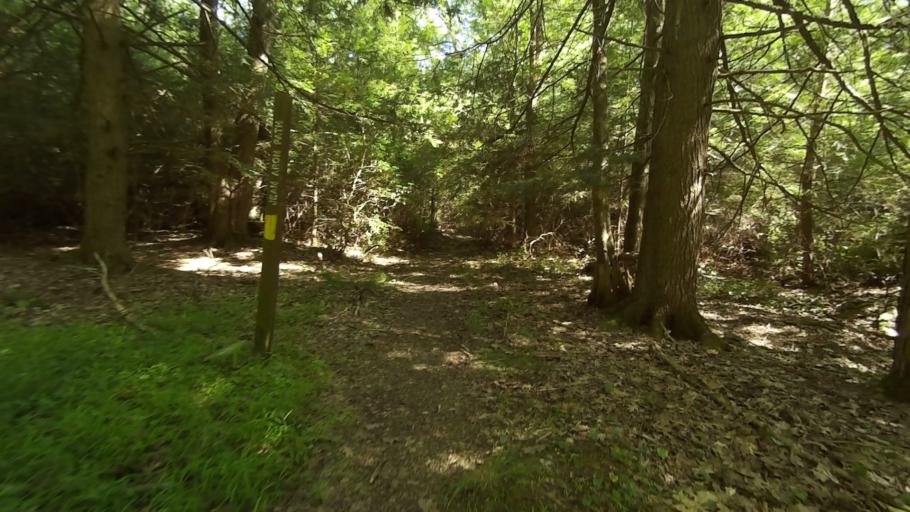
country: US
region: Pennsylvania
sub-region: Centre County
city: Boalsburg
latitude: 40.7397
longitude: -77.7537
